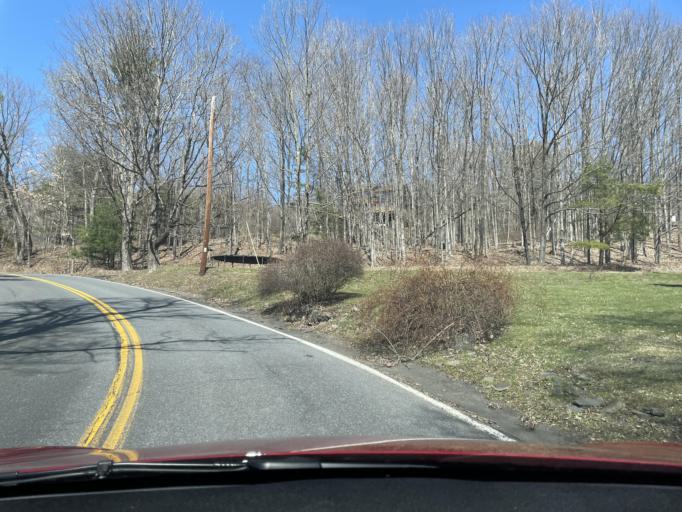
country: US
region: New York
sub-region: Ulster County
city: West Hurley
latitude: 42.0081
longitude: -74.1375
